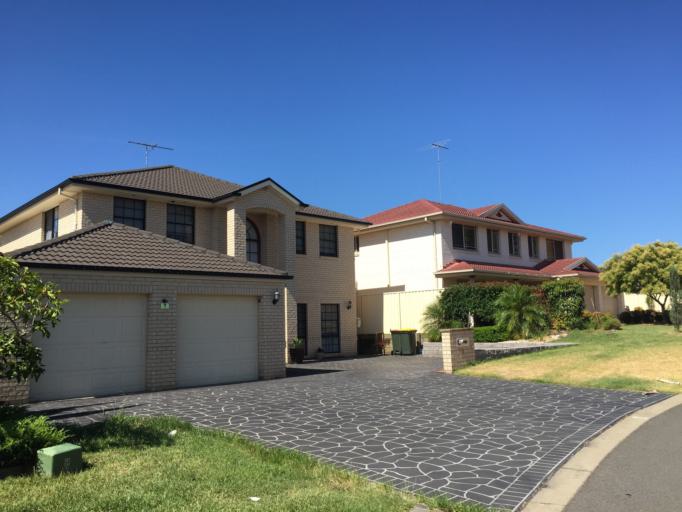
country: AU
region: New South Wales
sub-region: Blacktown
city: Stanhope Gardens
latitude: -33.7264
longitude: 150.9076
